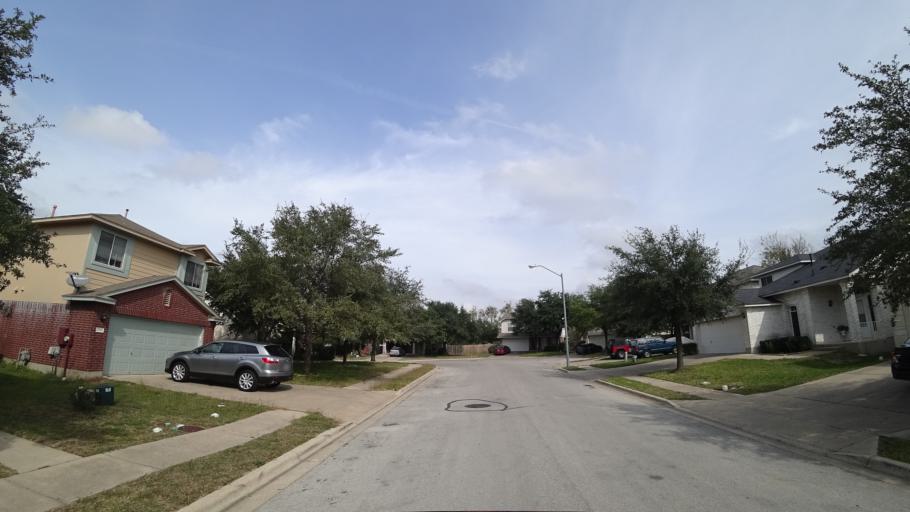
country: US
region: Texas
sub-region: Travis County
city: Windemere
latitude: 30.4387
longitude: -97.6563
